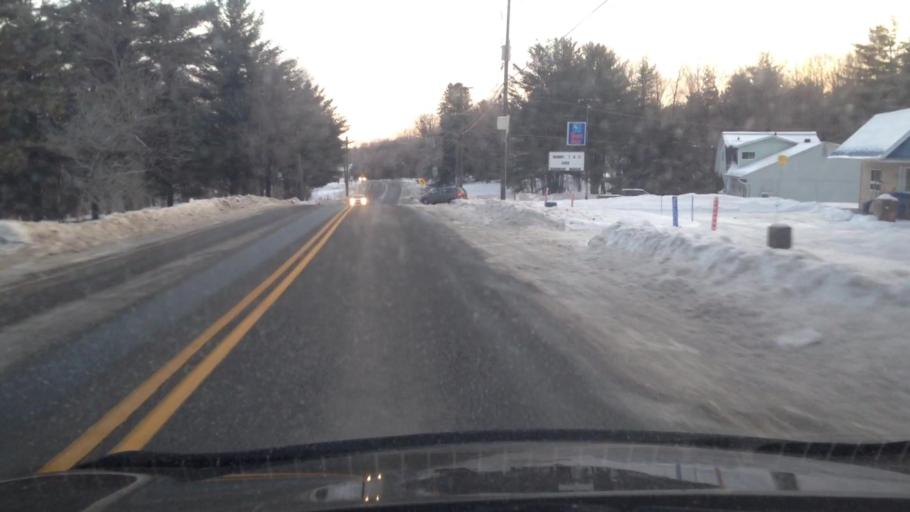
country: CA
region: Quebec
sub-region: Lanaudiere
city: Sainte-Julienne
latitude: 45.9488
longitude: -73.7342
